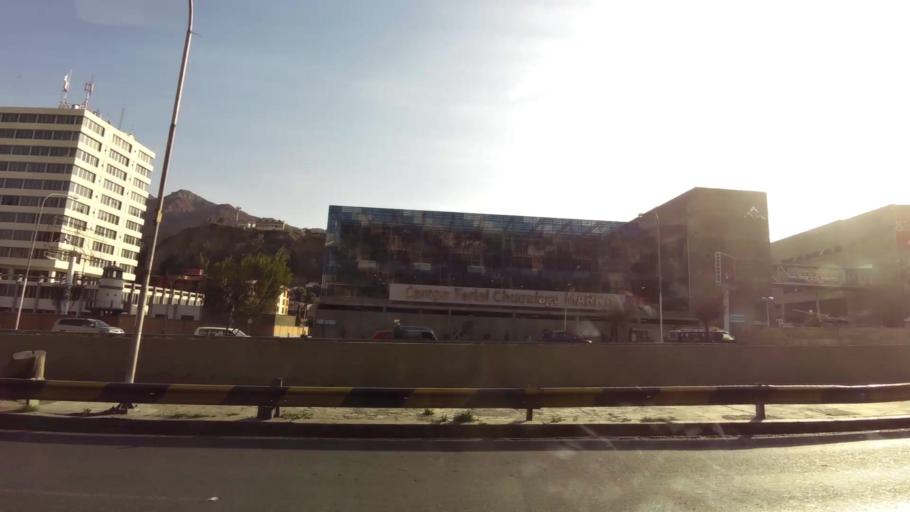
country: BO
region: La Paz
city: La Paz
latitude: -16.5376
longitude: -68.0953
